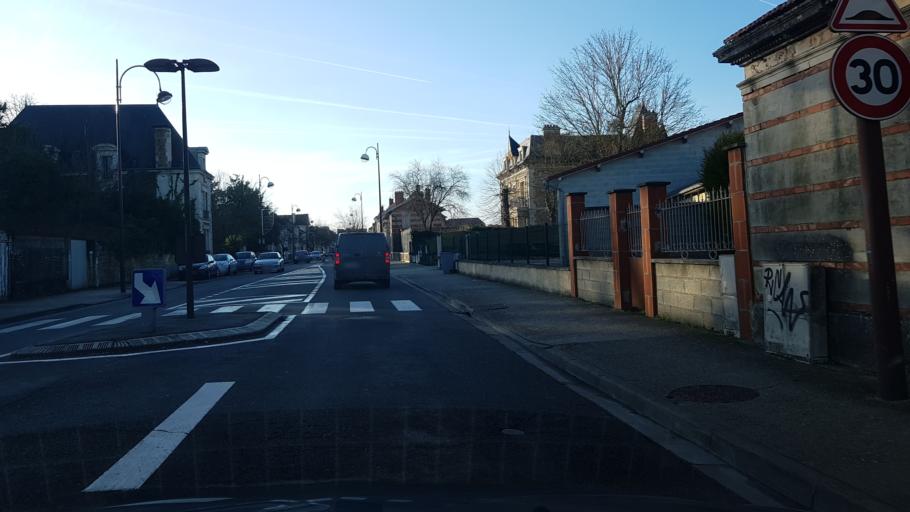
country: FR
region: Champagne-Ardenne
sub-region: Departement de la Marne
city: Vitry-le-Francois
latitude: 48.7292
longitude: 4.5932
